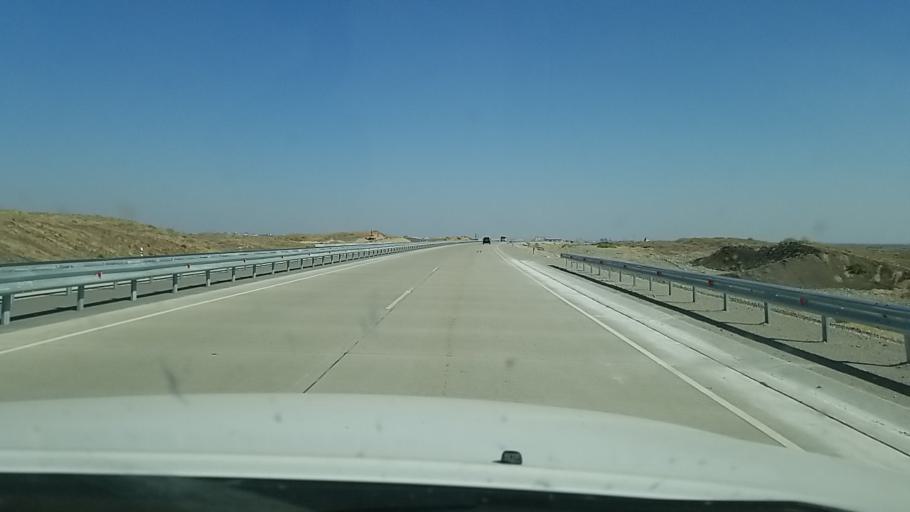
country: KZ
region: Almaty Oblysy
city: Zharkent
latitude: 44.1738
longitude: 80.3374
